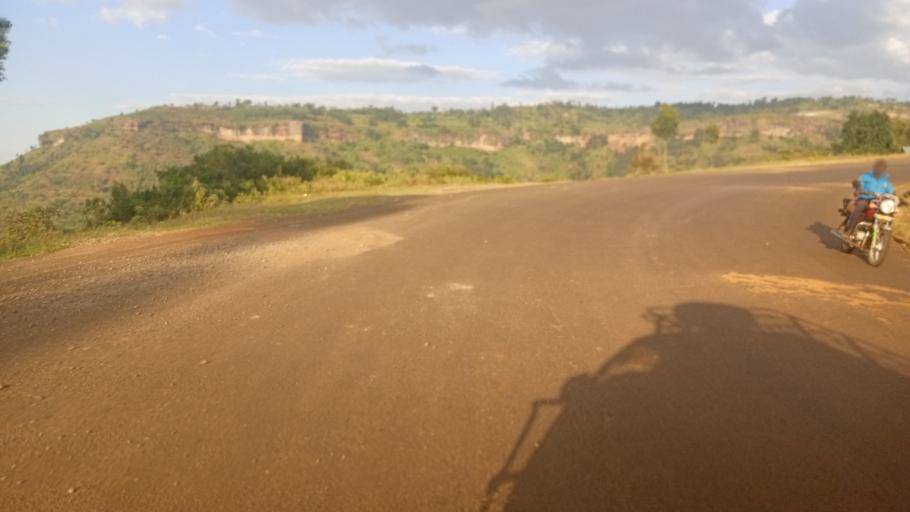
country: UG
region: Eastern Region
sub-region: Kapchorwa District
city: Kapchorwa
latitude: 1.3416
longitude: 34.3604
